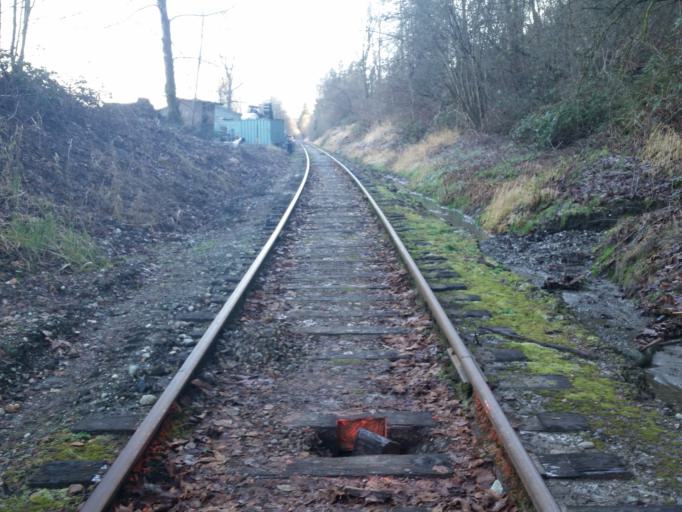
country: US
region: Washington
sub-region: King County
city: Woodinville
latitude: 47.7502
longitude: -122.1681
